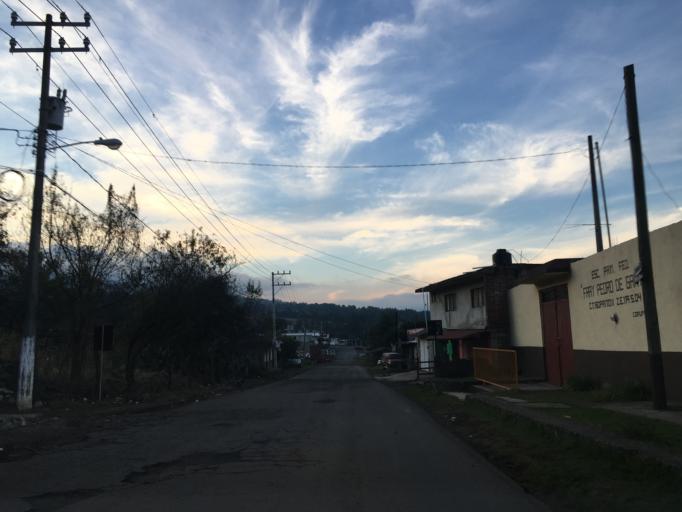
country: MX
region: Michoacan
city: Charapan
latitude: 19.6133
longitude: -102.2336
